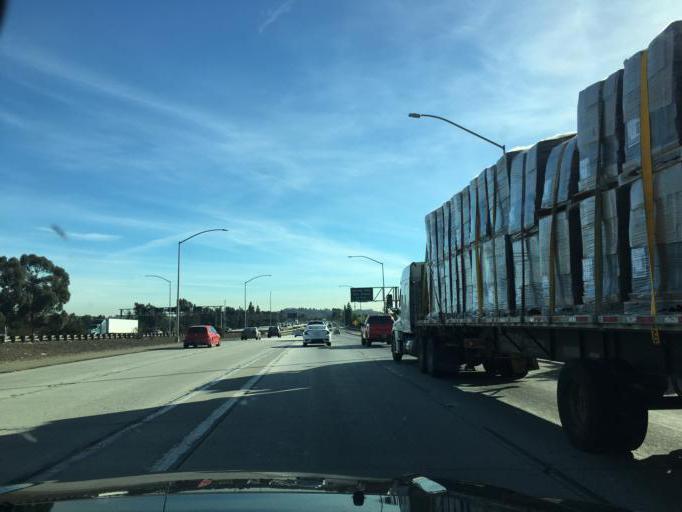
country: US
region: California
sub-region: Los Angeles County
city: San Dimas
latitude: 34.1172
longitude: -117.8245
